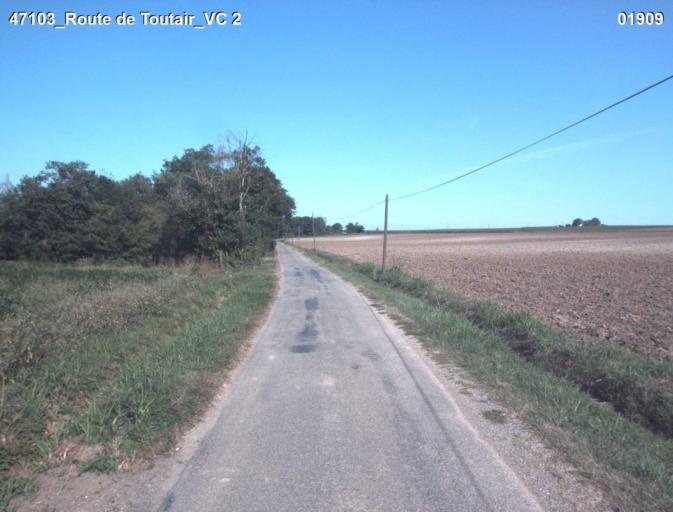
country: FR
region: Aquitaine
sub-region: Departement du Lot-et-Garonne
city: Nerac
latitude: 44.0721
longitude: 0.3335
